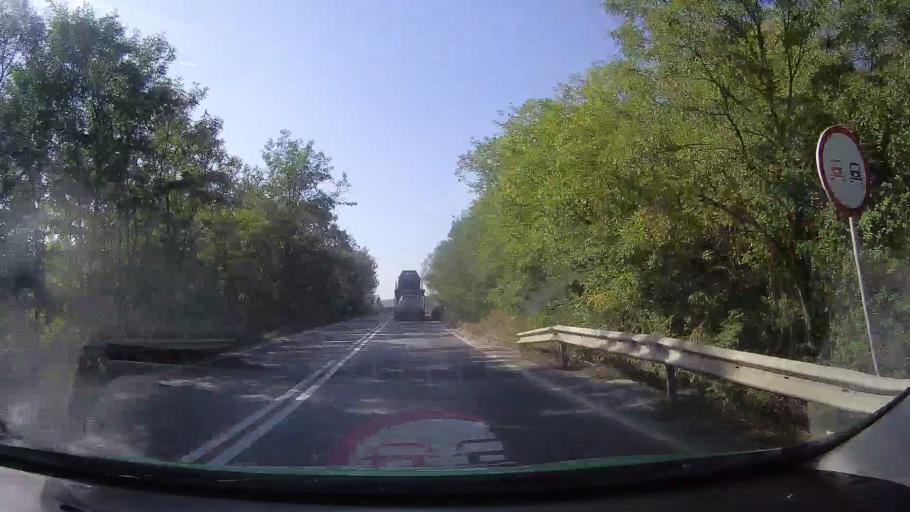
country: RO
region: Arad
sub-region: Comuna Conop
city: Conop
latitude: 46.1097
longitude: 21.8549
